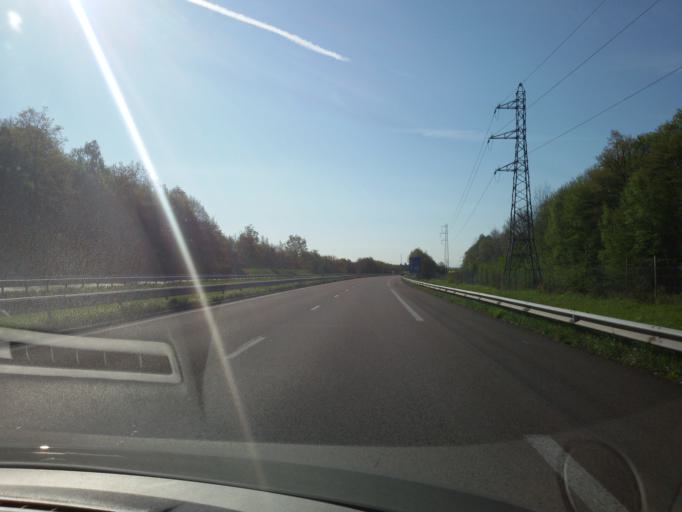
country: FR
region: Centre
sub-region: Departement du Loiret
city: Courtenay
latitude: 48.0713
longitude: 3.0726
